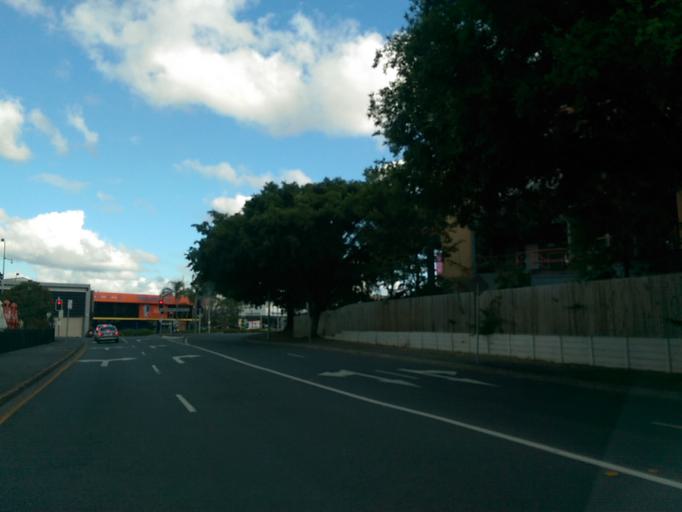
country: AU
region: Queensland
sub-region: Brisbane
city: Windsor
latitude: -27.4447
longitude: 153.0421
